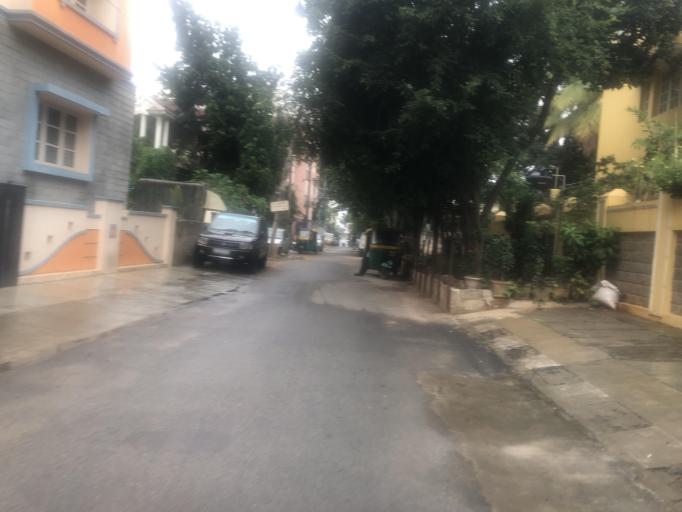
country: IN
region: Karnataka
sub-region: Bangalore Urban
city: Bangalore
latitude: 12.9396
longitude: 77.5384
